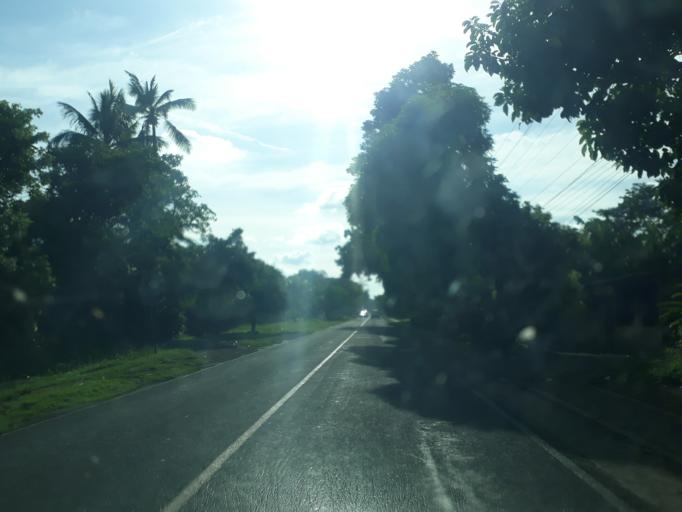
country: NI
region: Masaya
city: Masatepe
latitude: 11.9052
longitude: -86.1670
